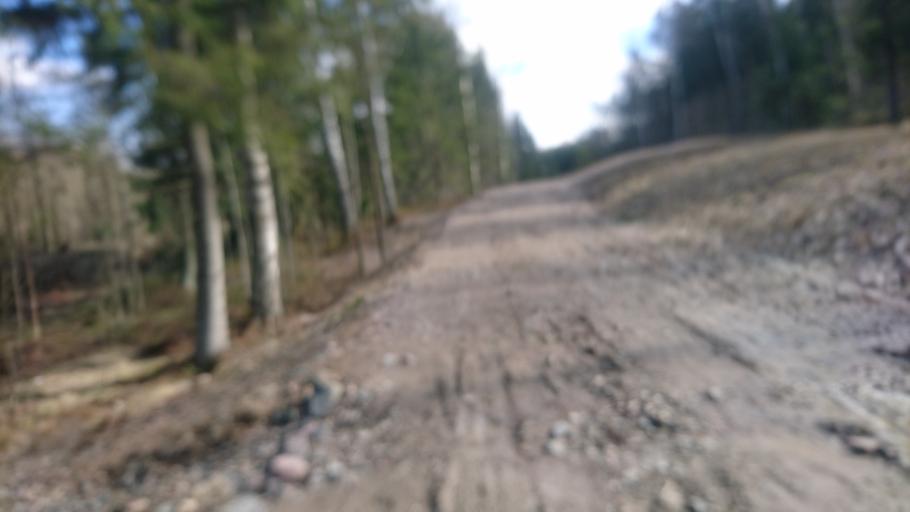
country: FI
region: Uusimaa
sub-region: Helsinki
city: Kauniainen
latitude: 60.2002
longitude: 24.7280
